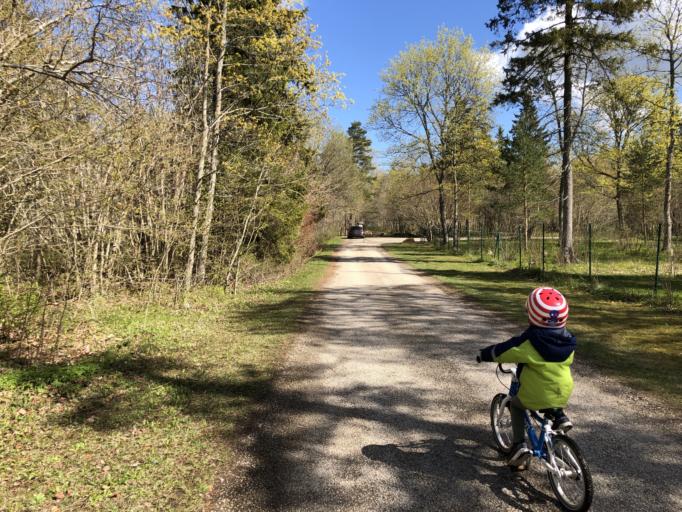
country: EE
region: Harju
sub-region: Harku vald
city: Tabasalu
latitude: 59.4390
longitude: 24.5289
